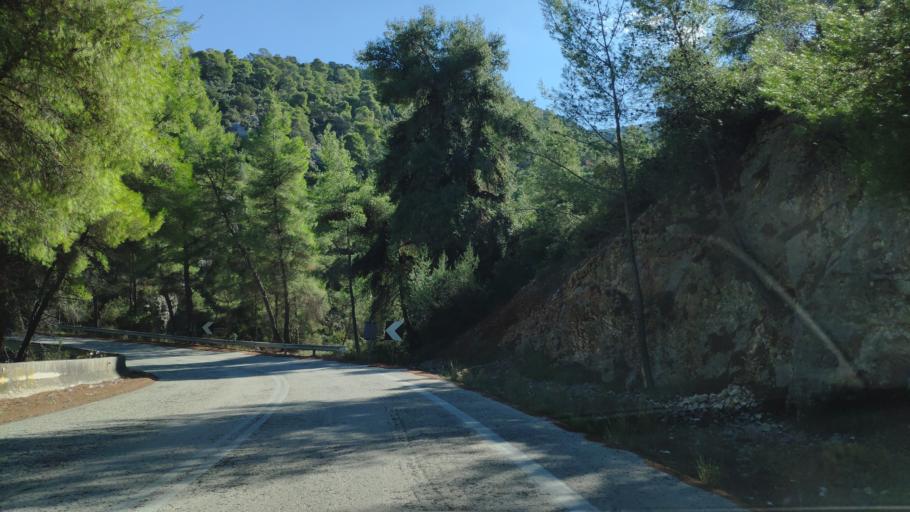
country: GR
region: Peloponnese
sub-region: Nomos Korinthias
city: Sofikon
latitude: 37.8271
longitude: 23.0653
